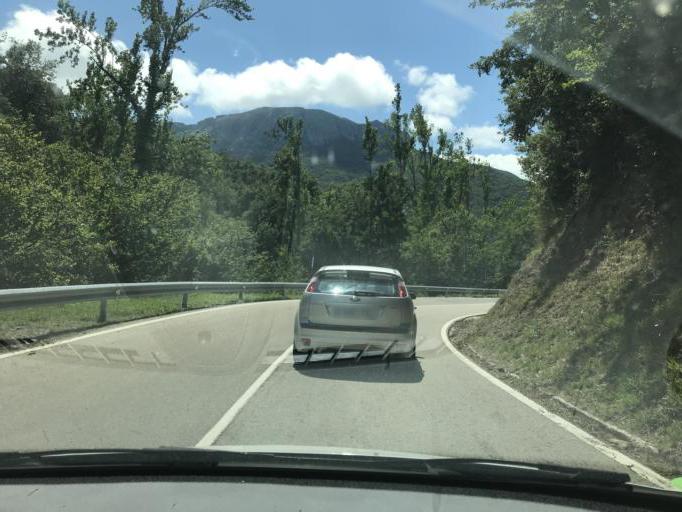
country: ES
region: Cantabria
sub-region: Provincia de Cantabria
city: Cabezon de Liebana
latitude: 43.0782
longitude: -4.4872
